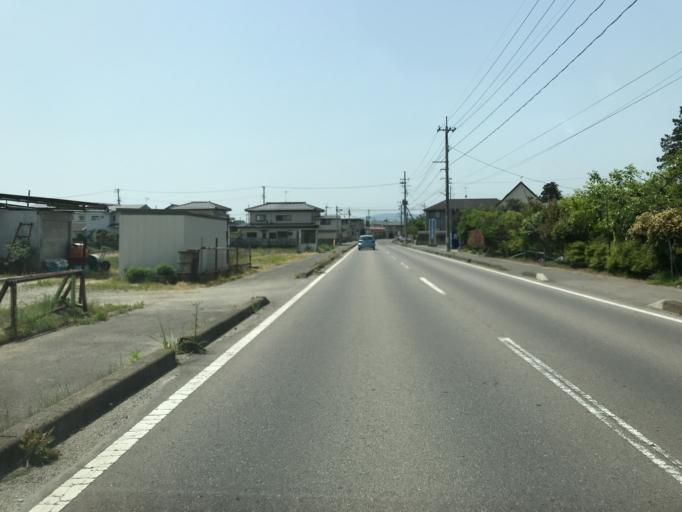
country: JP
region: Fukushima
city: Fukushima-shi
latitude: 37.7756
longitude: 140.4248
